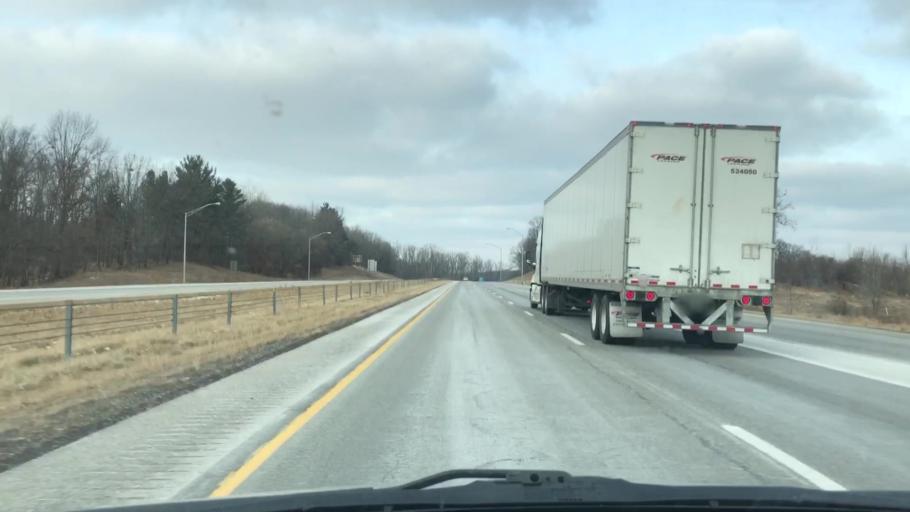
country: US
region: Indiana
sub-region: Steuben County
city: Angola
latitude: 41.6379
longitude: -85.0479
